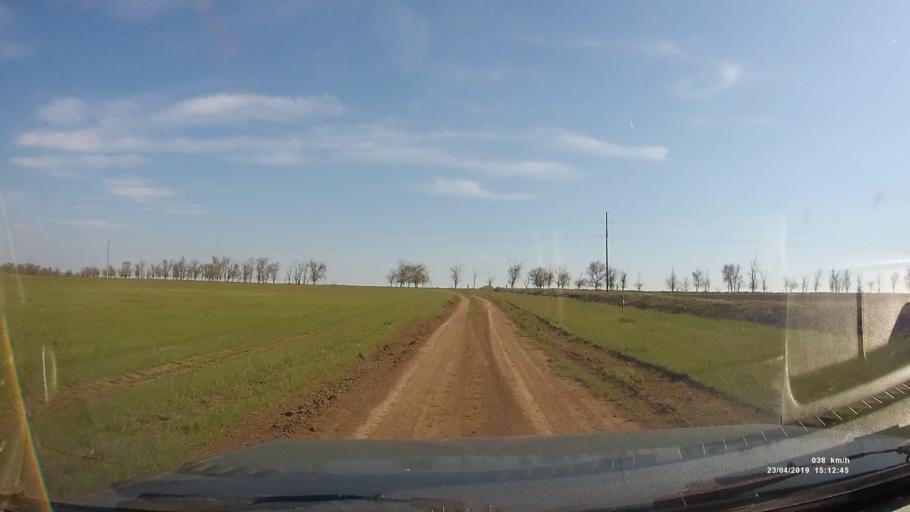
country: RU
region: Rostov
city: Remontnoye
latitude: 46.5422
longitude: 42.9509
